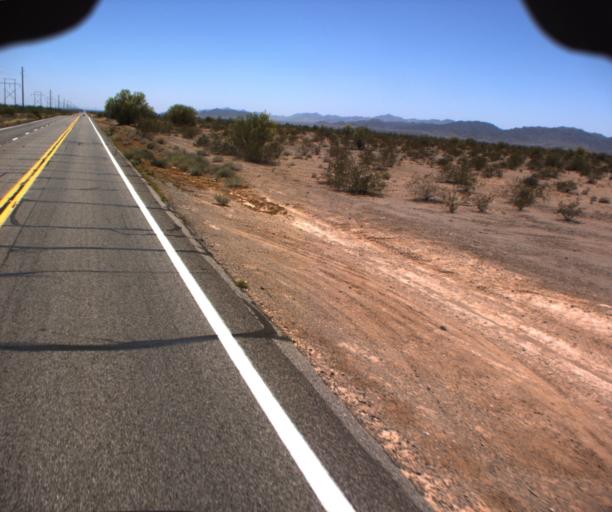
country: US
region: Arizona
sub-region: La Paz County
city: Quartzsite
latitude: 33.7842
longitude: -114.2170
